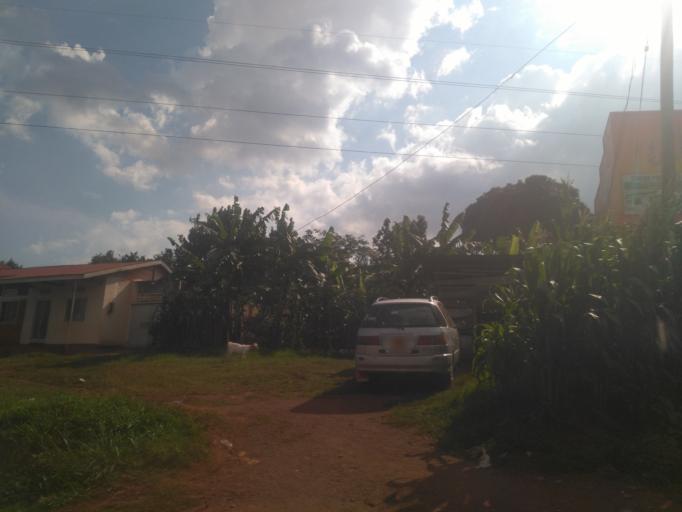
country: UG
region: Central Region
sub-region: Wakiso District
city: Kajansi
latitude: 0.2717
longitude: 32.4626
